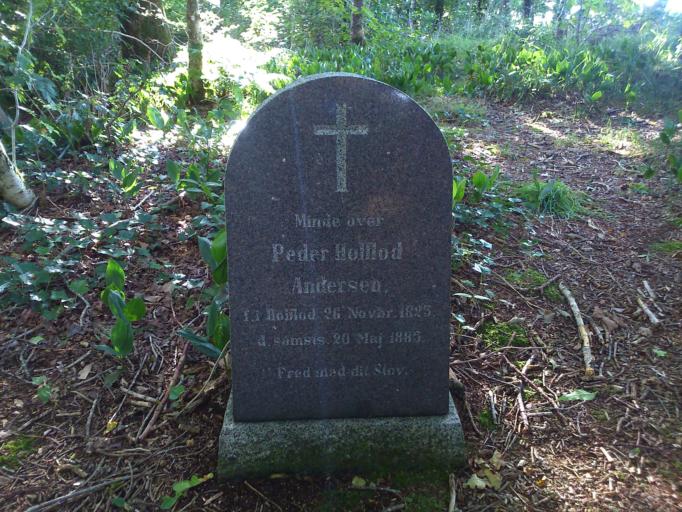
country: DK
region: Central Jutland
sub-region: Herning Kommune
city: Snejbjerg
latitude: 56.1875
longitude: 8.8471
